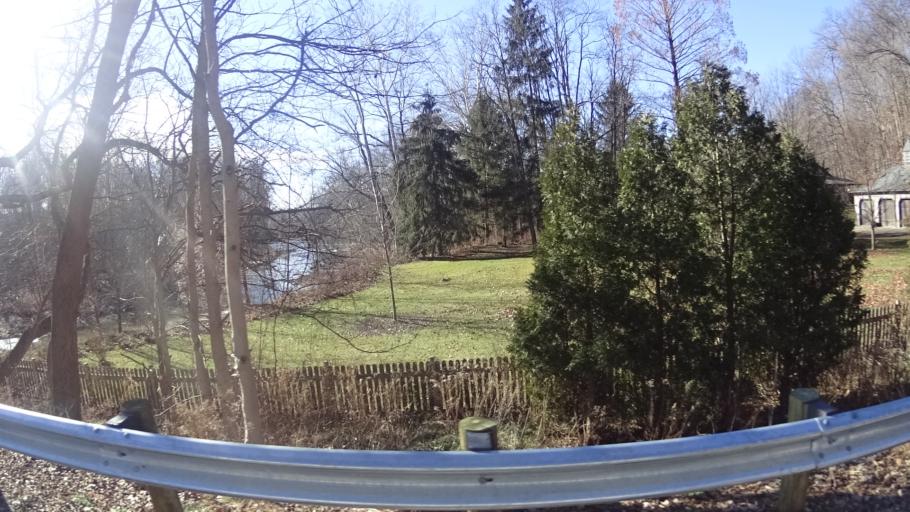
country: US
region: Ohio
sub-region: Lorain County
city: Vermilion
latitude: 41.3493
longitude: -82.3453
